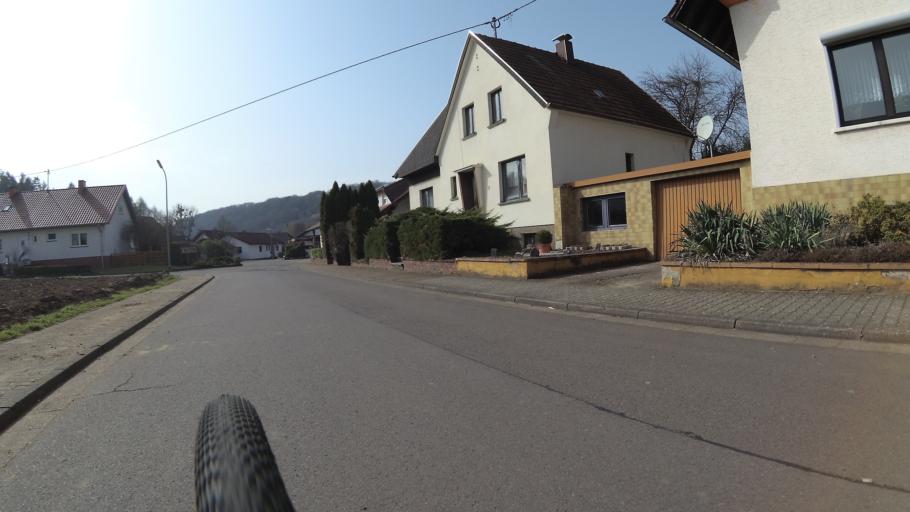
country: DE
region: Saarland
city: Beckingen
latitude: 49.4386
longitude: 6.7422
